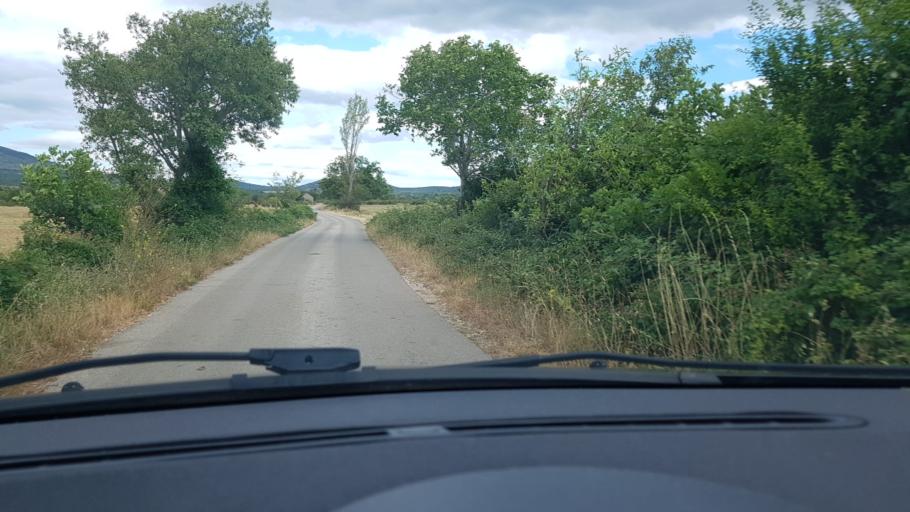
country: HR
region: Sibensko-Kniniska
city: Kistanje
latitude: 44.1096
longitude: 15.9272
